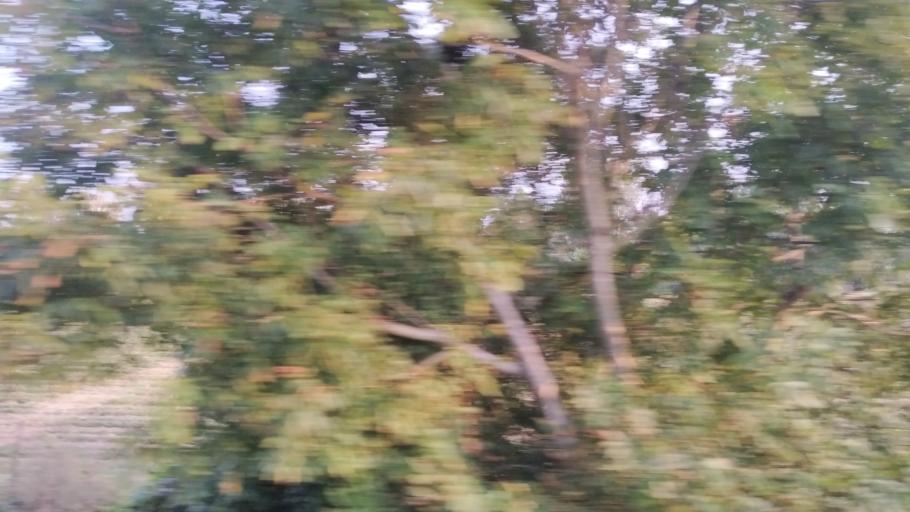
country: HU
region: Pest
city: Pomaz
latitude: 47.6473
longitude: 19.0405
